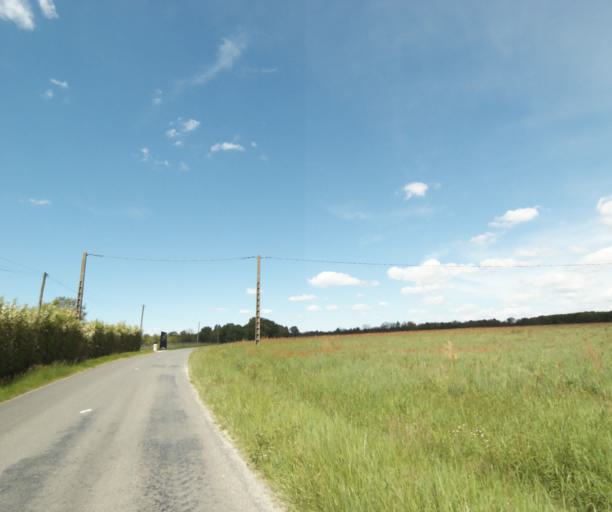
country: FR
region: Poitou-Charentes
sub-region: Departement de la Charente-Maritime
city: Burie
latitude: 45.7542
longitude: -0.4615
